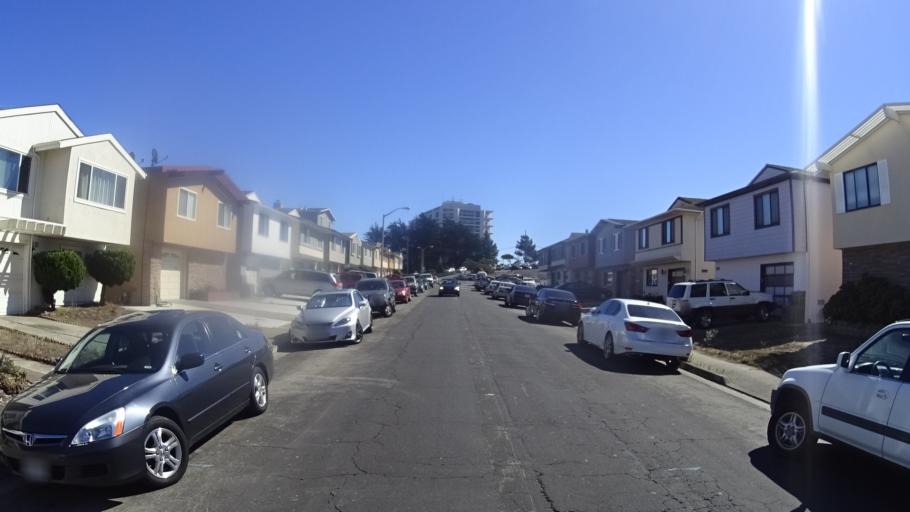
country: US
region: California
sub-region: San Mateo County
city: Broadmoor
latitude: 37.6807
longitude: -122.4775
